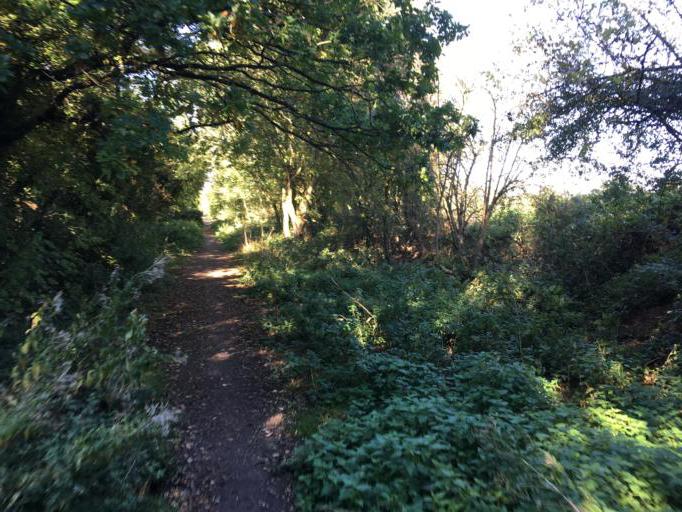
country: GB
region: England
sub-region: Solihull
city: Balsall Common
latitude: 52.3880
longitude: -1.6227
